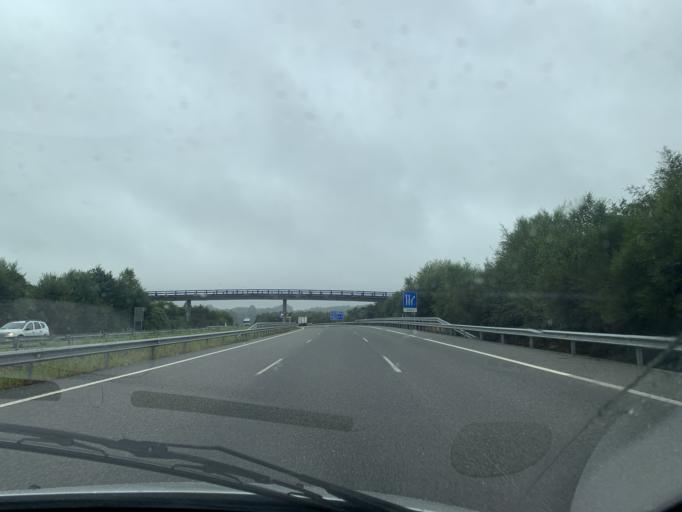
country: ES
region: Galicia
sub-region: Provincia de Lugo
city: Vilalba
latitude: 43.3209
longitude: -7.6759
